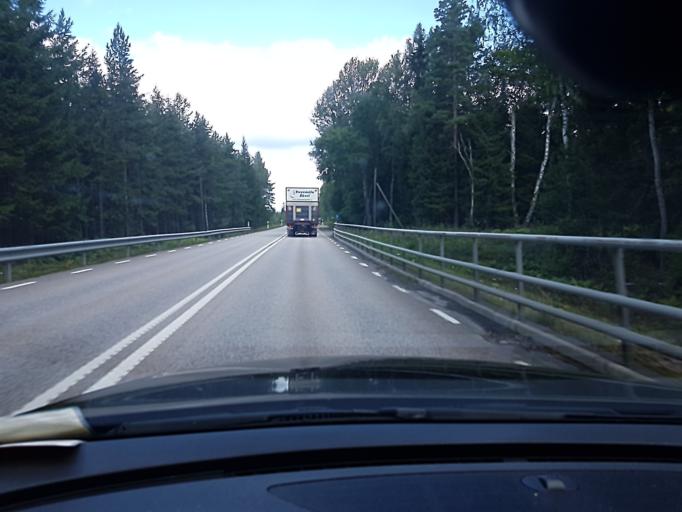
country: SE
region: Kronoberg
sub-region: Lessebo Kommun
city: Lessebo
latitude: 56.7367
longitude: 15.2805
